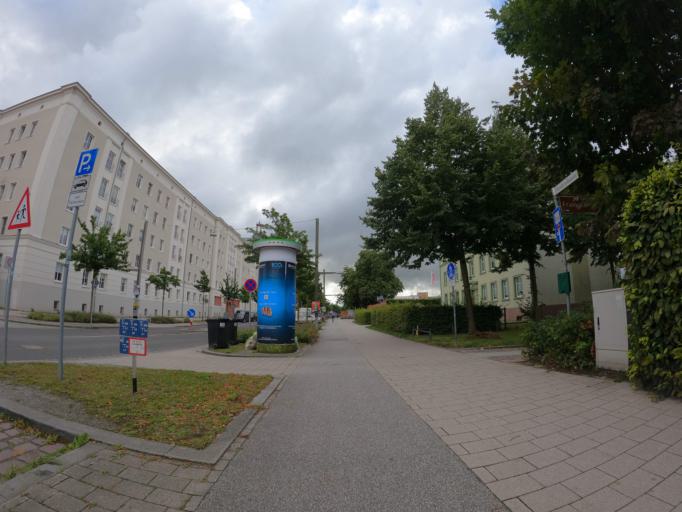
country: DE
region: Mecklenburg-Vorpommern
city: Stralsund
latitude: 54.3110
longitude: 13.0973
